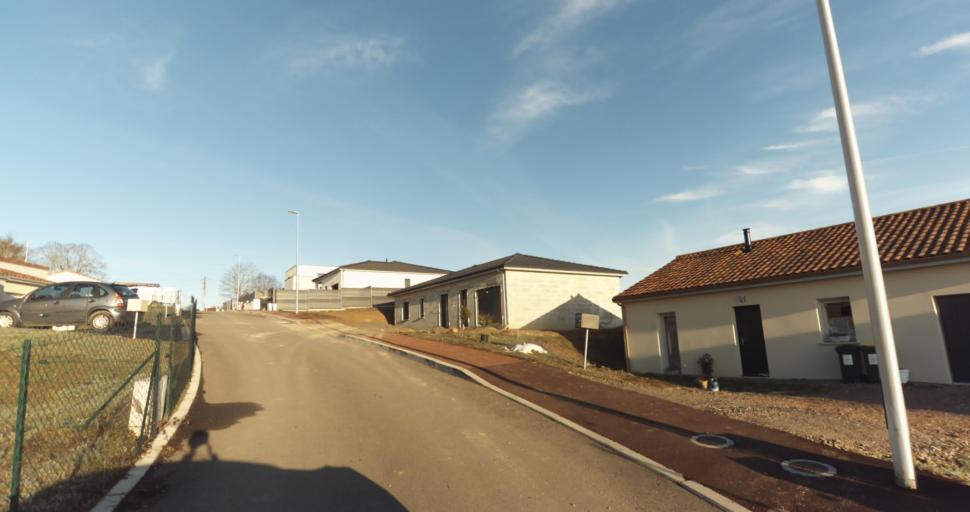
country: FR
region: Limousin
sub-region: Departement de la Haute-Vienne
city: Aixe-sur-Vienne
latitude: 45.8008
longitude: 1.1472
